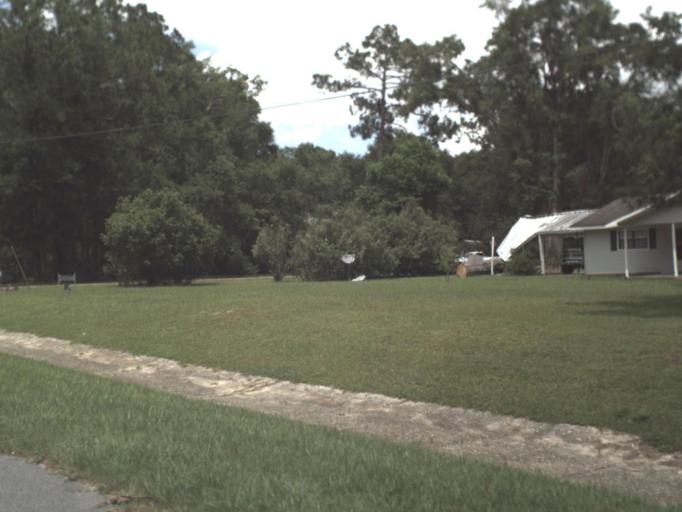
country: US
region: Florida
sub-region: Madison County
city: Madison
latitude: 30.6006
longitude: -83.3521
